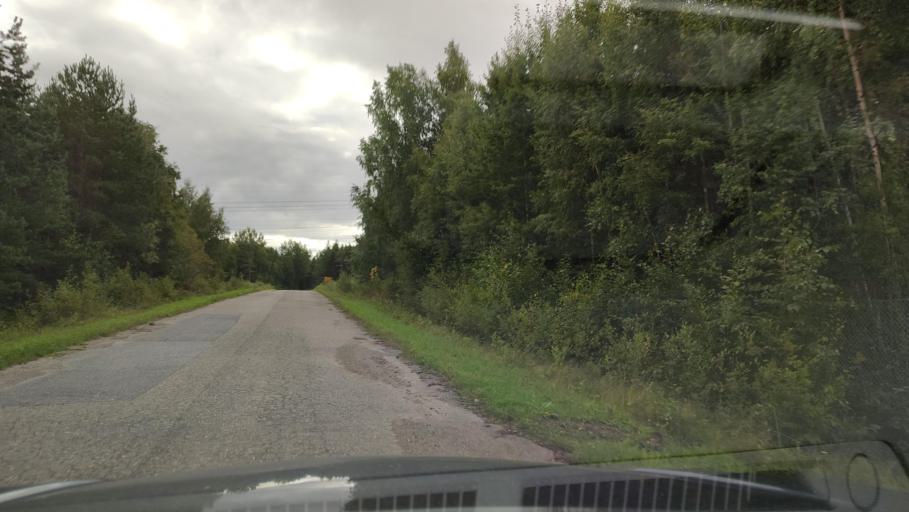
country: FI
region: Ostrobothnia
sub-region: Sydosterbotten
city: Kristinestad
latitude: 62.2565
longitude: 21.3355
